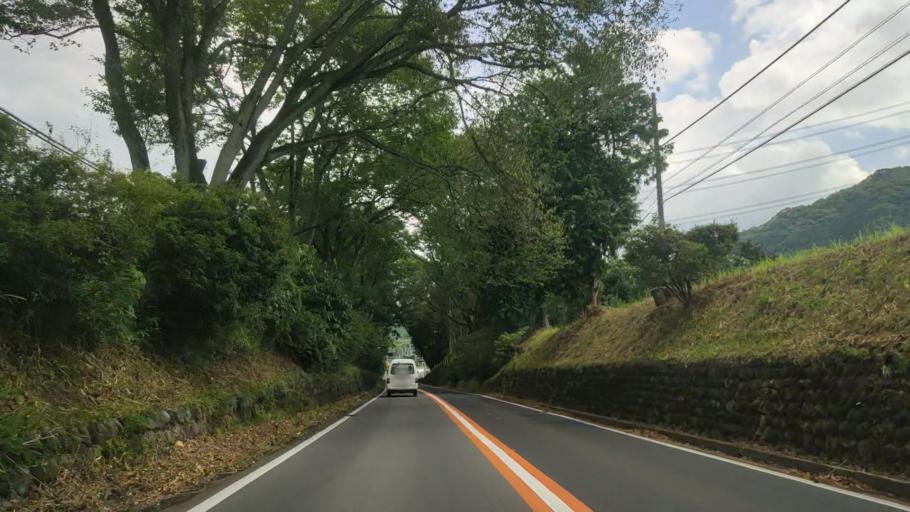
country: JP
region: Tochigi
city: Utsunomiya-shi
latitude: 36.6706
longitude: 139.8123
